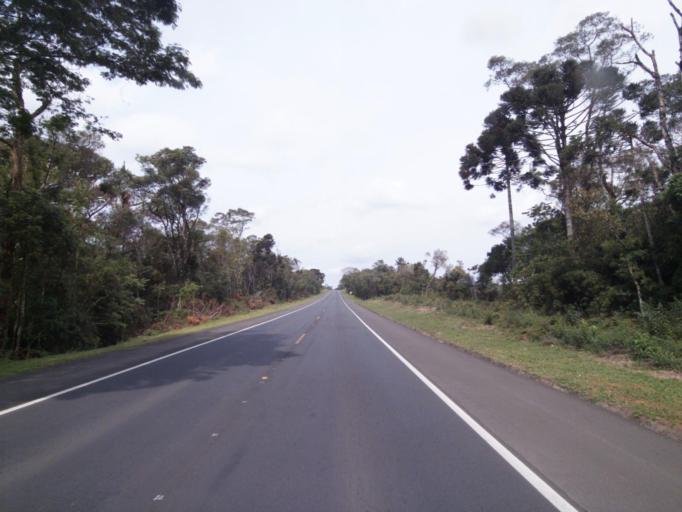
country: BR
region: Parana
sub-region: Irati
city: Irati
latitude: -25.4692
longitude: -50.5038
